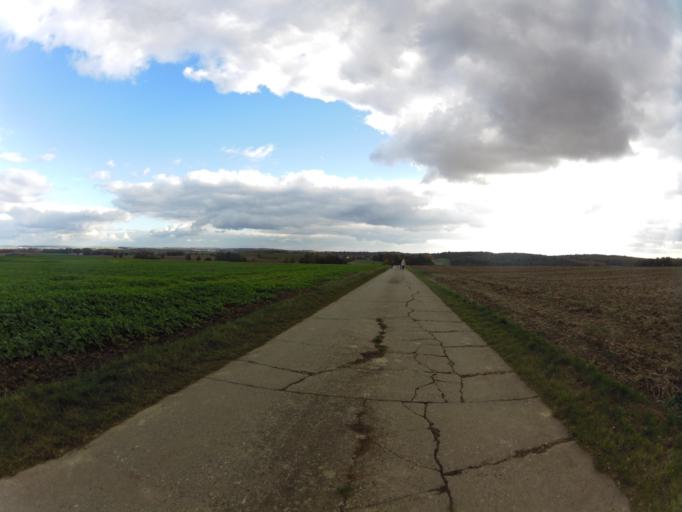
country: DE
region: Bavaria
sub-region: Regierungsbezirk Unterfranken
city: Kurnach
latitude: 49.8688
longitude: 10.0022
